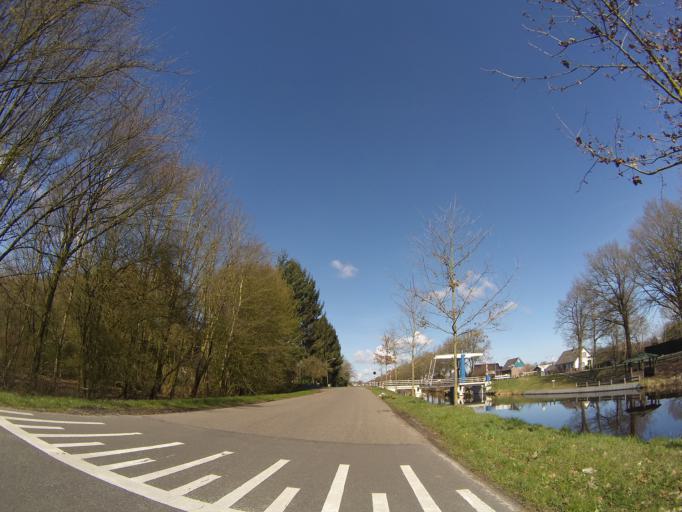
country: NL
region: Drenthe
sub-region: Gemeente Emmen
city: Klazienaveen
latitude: 52.7399
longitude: 6.9444
